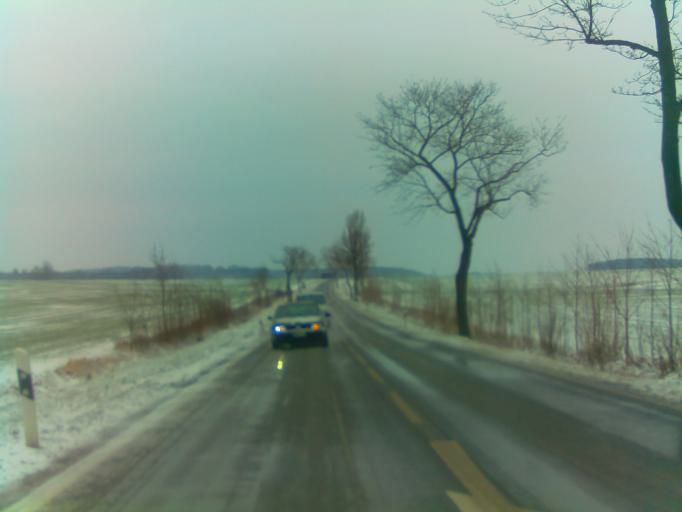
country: DE
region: Thuringia
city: Alkersleben
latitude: 50.8138
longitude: 11.0264
